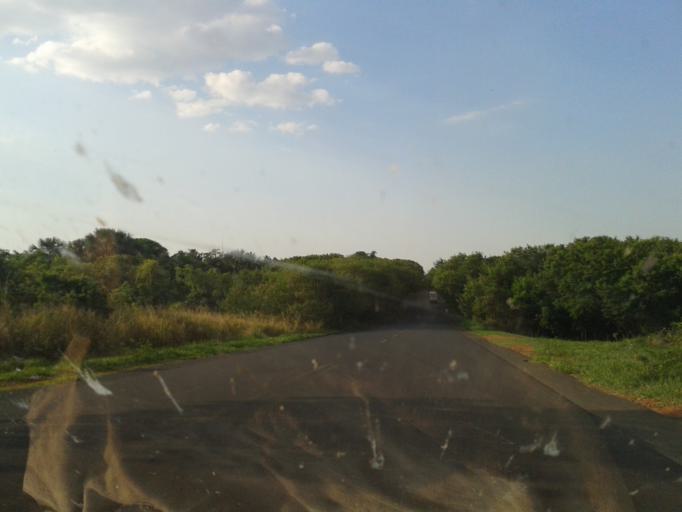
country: BR
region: Minas Gerais
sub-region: Uberlandia
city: Uberlandia
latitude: -18.9543
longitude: -48.3070
